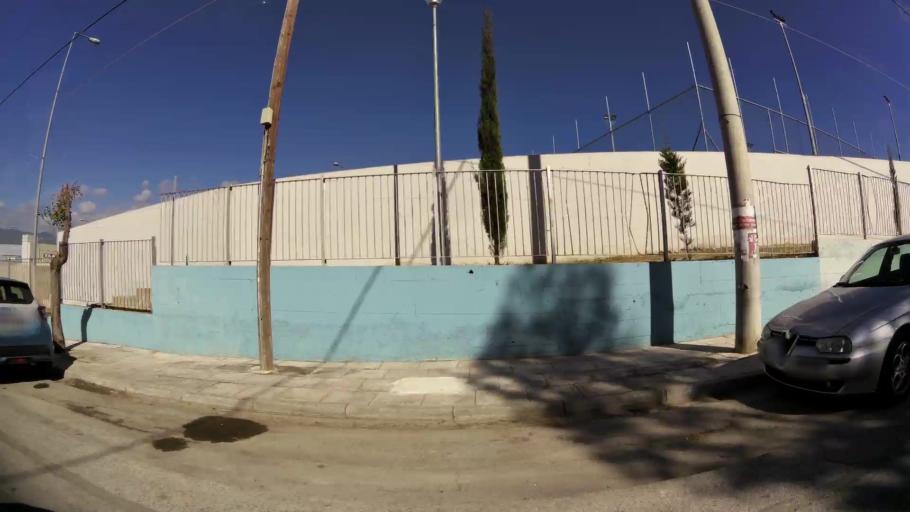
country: GR
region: Attica
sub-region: Nomarchia Athinas
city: Metamorfosi
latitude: 38.0690
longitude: 23.7712
